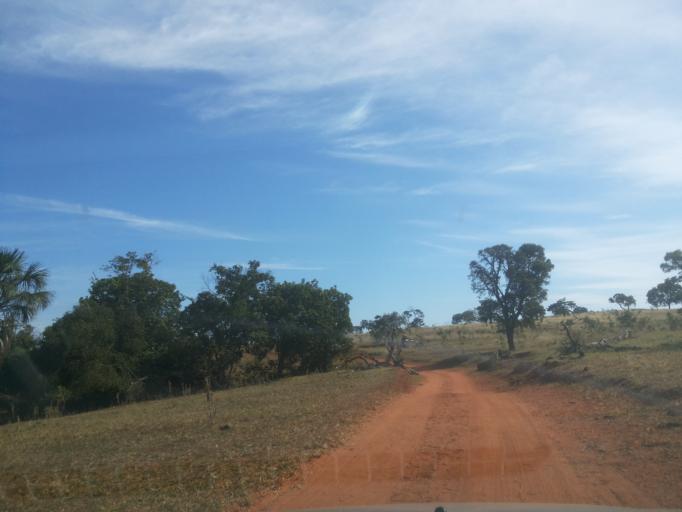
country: BR
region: Minas Gerais
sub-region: Ituiutaba
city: Ituiutaba
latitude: -19.1116
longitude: -49.4141
